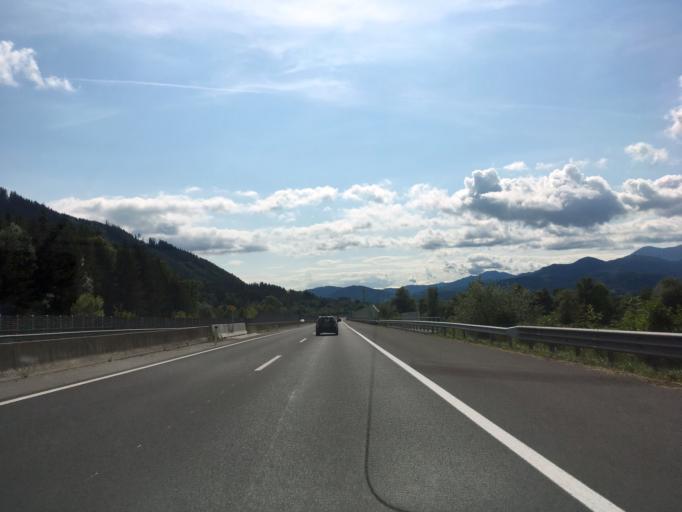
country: AT
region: Styria
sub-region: Politischer Bezirk Bruck-Muerzzuschlag
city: Sankt Marein im Muerztal
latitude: 47.4693
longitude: 15.3798
